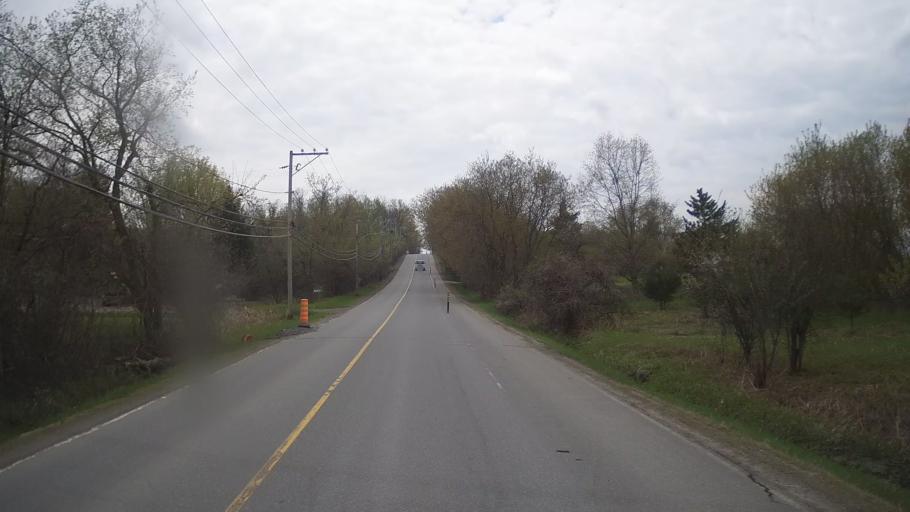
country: CA
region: Quebec
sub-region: Monteregie
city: Hudson
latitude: 45.4449
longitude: -74.1685
